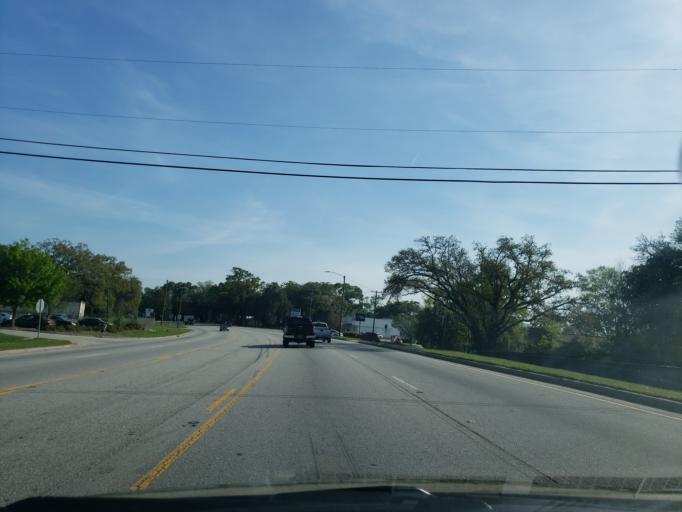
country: US
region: Georgia
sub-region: Chatham County
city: Garden City
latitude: 32.0868
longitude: -81.1974
